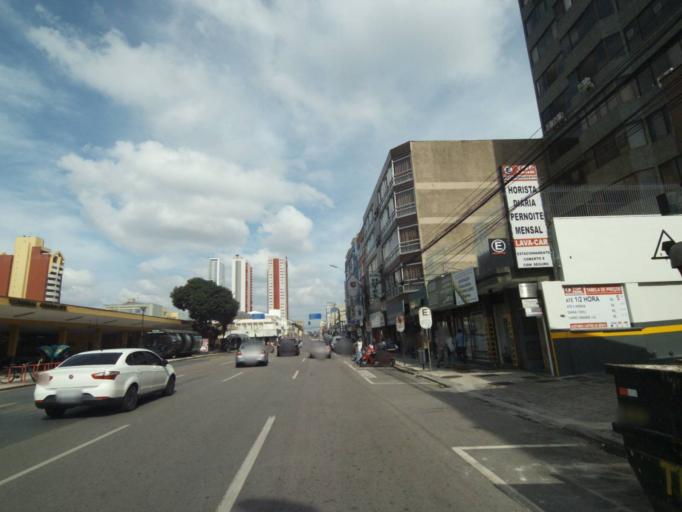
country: BR
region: Parana
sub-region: Curitiba
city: Curitiba
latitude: -25.4325
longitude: -49.2656
